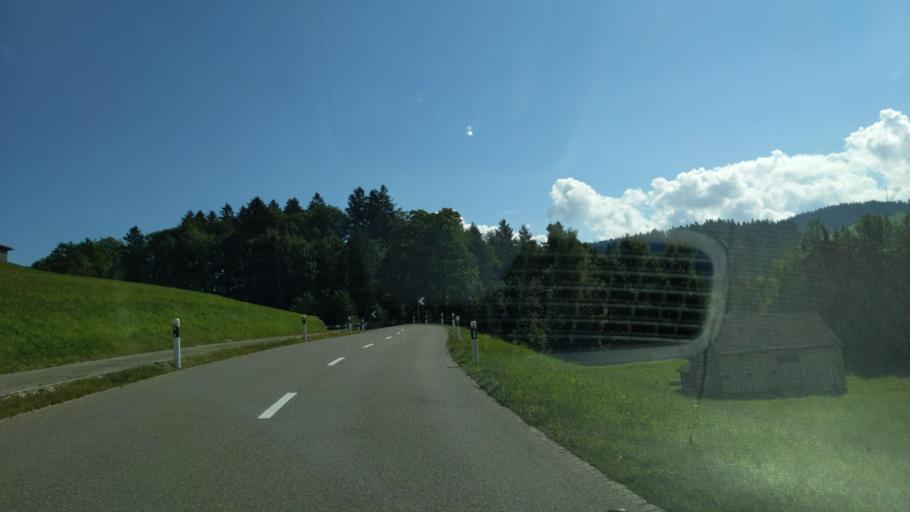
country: CH
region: Saint Gallen
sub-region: Wahlkreis Toggenburg
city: Sankt Peterzell
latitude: 47.3187
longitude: 9.1895
